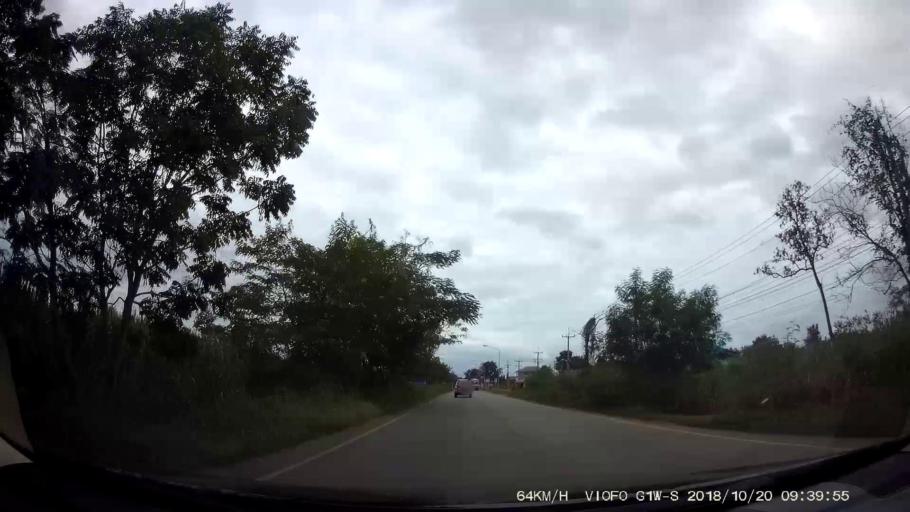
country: TH
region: Chaiyaphum
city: Kaset Sombun
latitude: 16.4386
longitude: 101.9634
